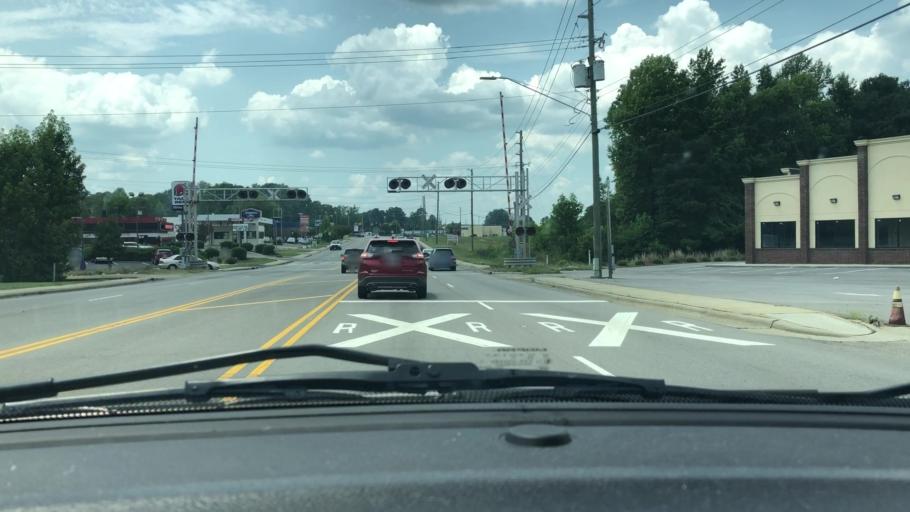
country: US
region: North Carolina
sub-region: Lee County
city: Sanford
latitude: 35.4602
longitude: -79.1574
